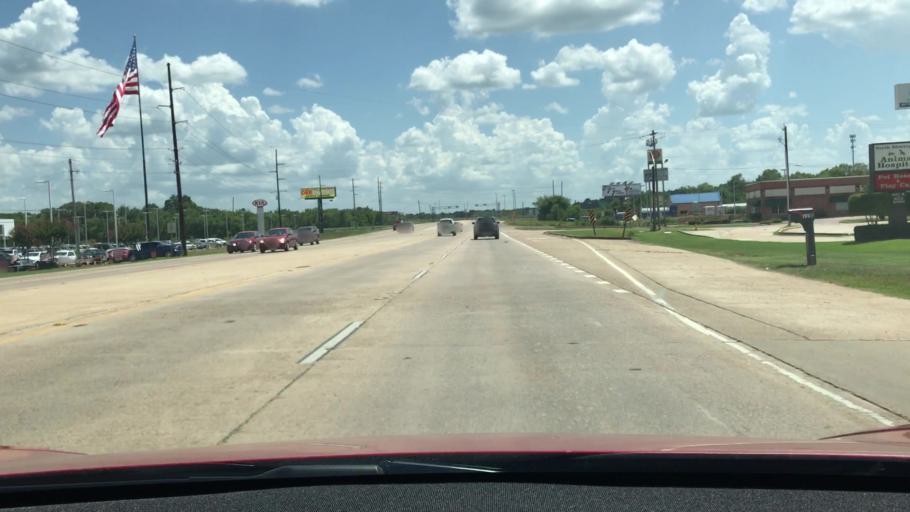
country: US
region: Louisiana
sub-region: Bossier Parish
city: Bossier City
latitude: 32.4187
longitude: -93.7227
